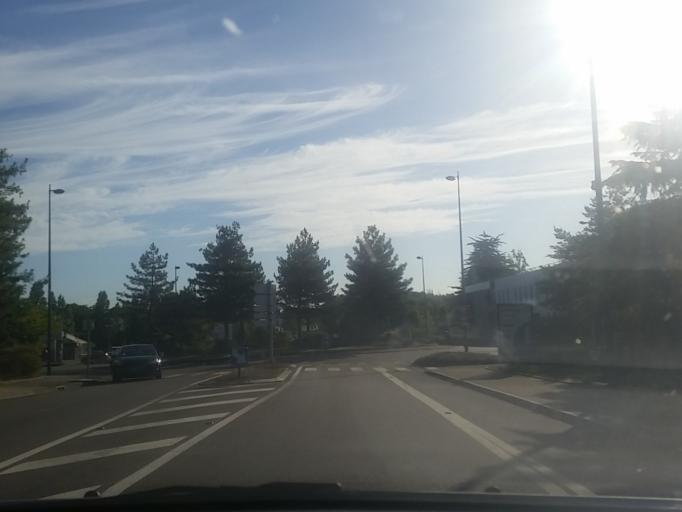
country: FR
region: Pays de la Loire
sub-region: Departement de la Loire-Atlantique
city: Bouguenais
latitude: 47.1754
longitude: -1.6232
